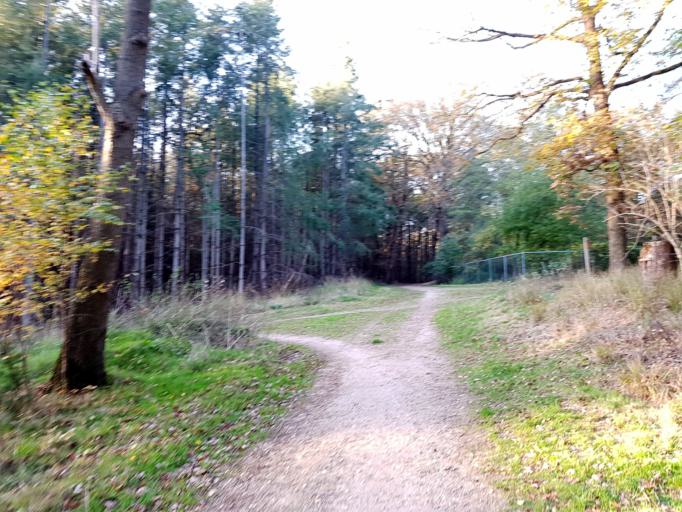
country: NL
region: Gelderland
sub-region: Gemeente Groesbeek
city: Berg en Dal
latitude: 51.8015
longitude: 5.8922
